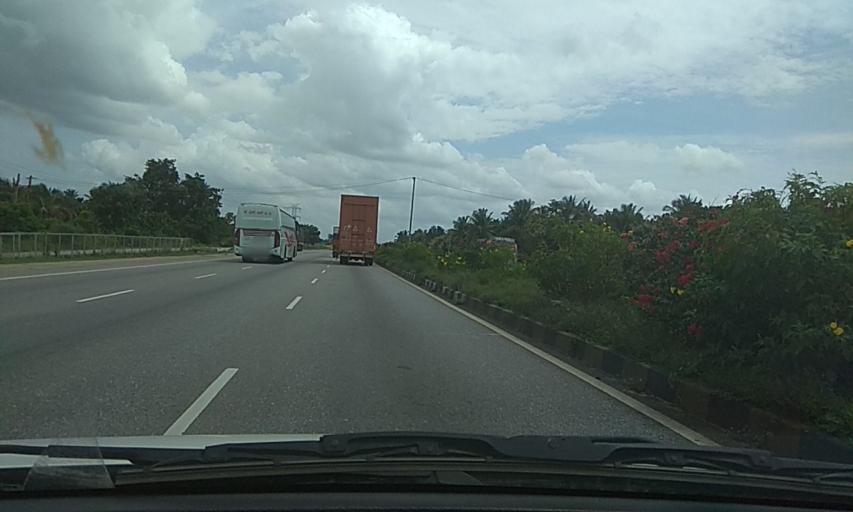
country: IN
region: Karnataka
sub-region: Tumkur
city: Tumkur
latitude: 13.5018
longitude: 77.0096
